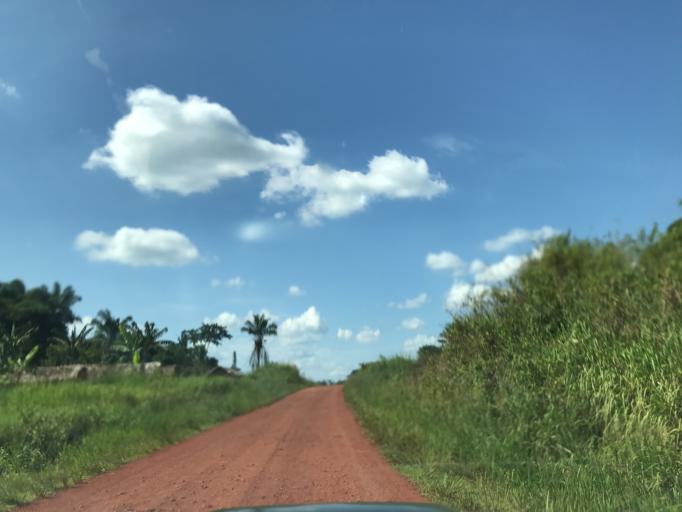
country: CD
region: Eastern Province
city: Kisangani
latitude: 1.2133
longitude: 25.2660
